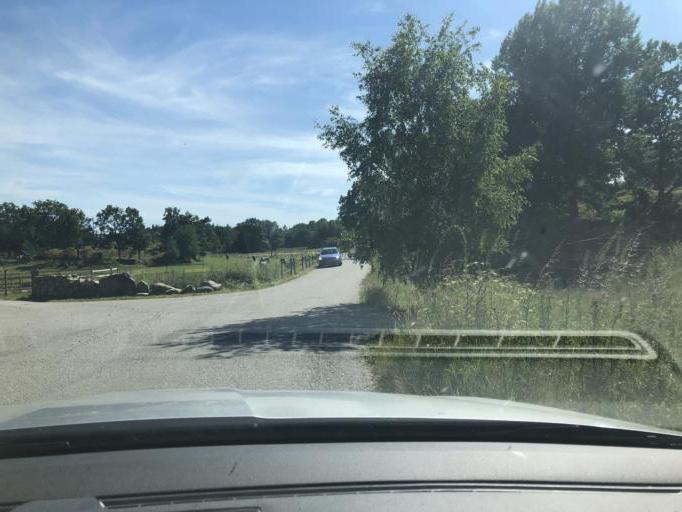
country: SE
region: Blekinge
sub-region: Karlshamns Kommun
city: Morrum
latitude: 56.1604
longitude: 14.8012
